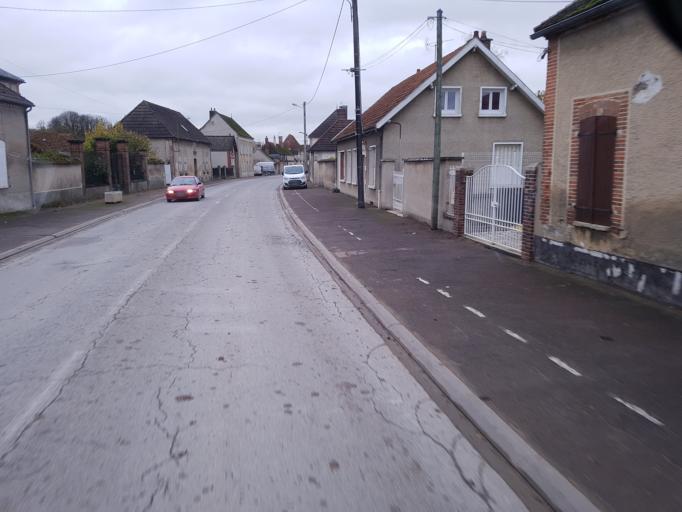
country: FR
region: Champagne-Ardenne
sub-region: Departement de la Marne
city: Saint-Just-Sauvage
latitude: 48.5849
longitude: 3.8182
